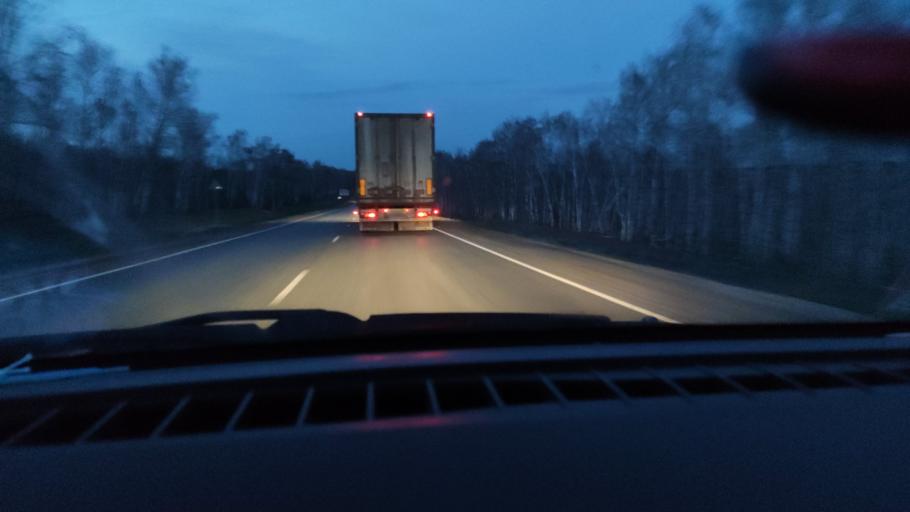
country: RU
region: Saratov
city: Sennoy
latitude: 52.1240
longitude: 46.8506
